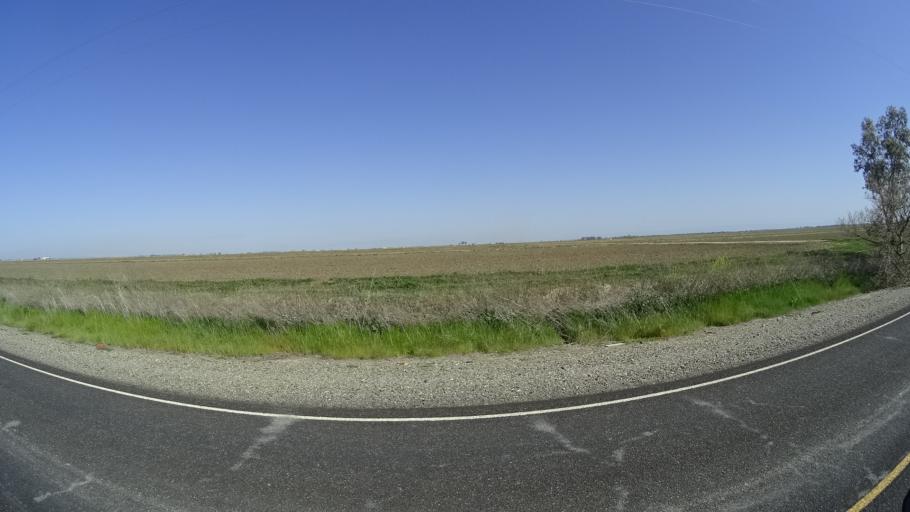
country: US
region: California
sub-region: Glenn County
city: Willows
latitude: 39.4577
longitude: -122.0540
